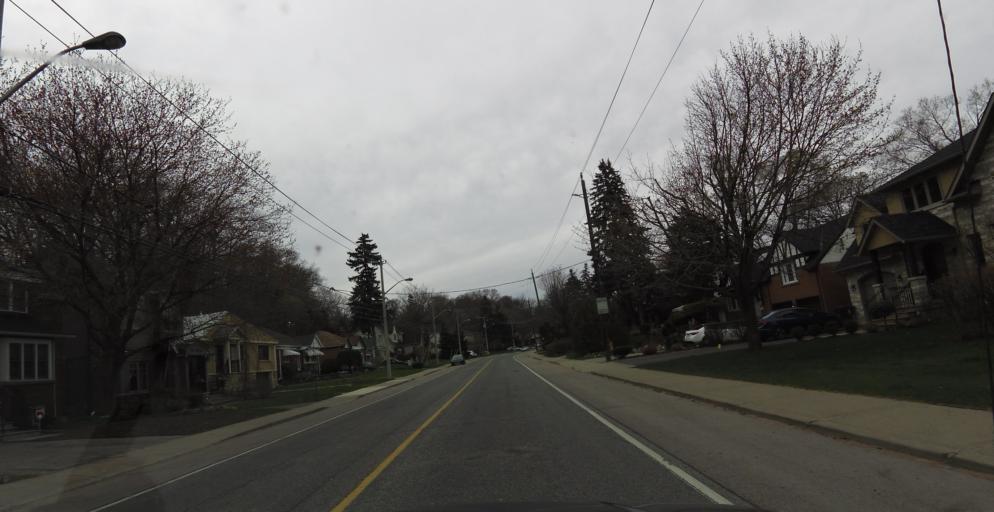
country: CA
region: Ontario
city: Toronto
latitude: 43.6424
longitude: -79.4805
